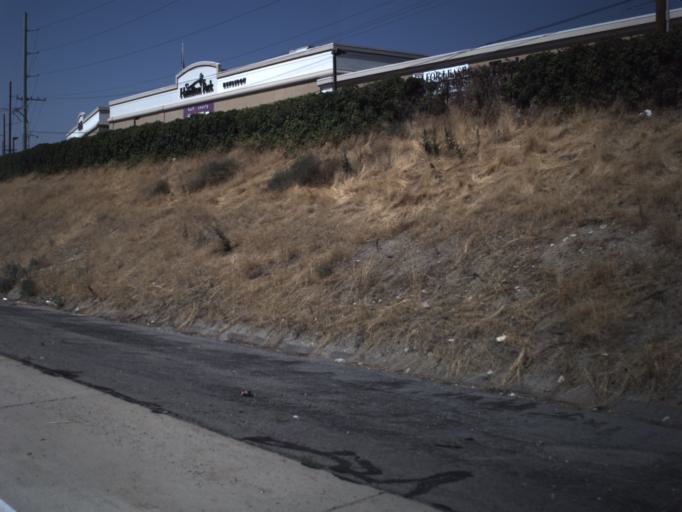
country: US
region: Utah
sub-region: Salt Lake County
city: Midvale
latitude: 40.6319
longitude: -111.8858
